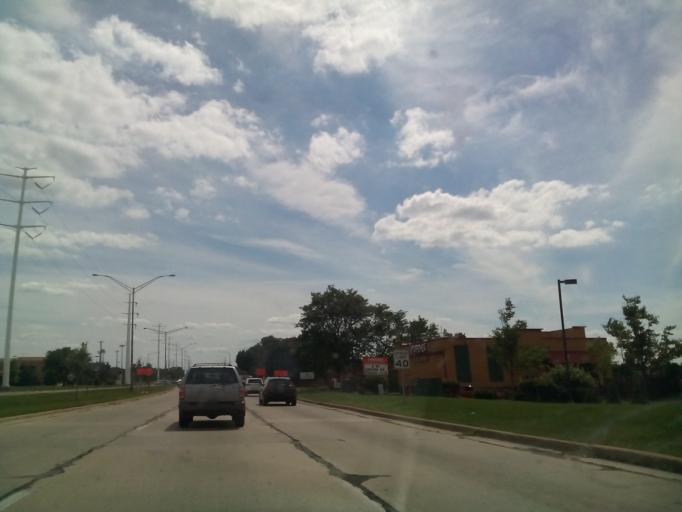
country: US
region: Illinois
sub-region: DuPage County
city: Naperville
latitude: 41.7583
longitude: -88.2061
